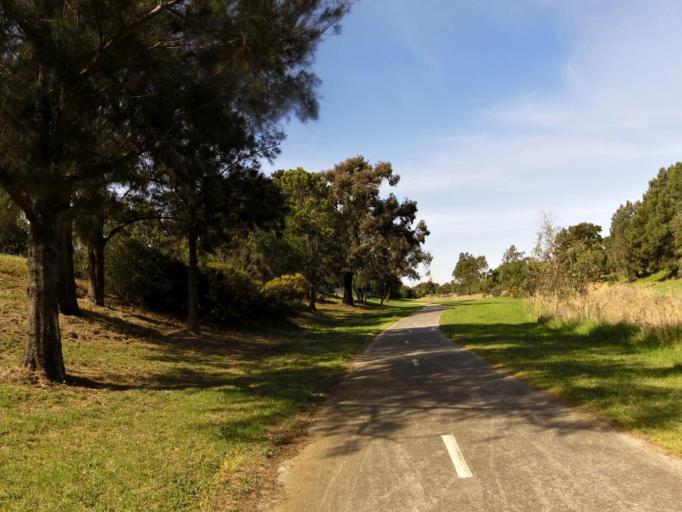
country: AU
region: Victoria
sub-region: Brimbank
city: Deer Park
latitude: -37.7770
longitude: 144.7984
